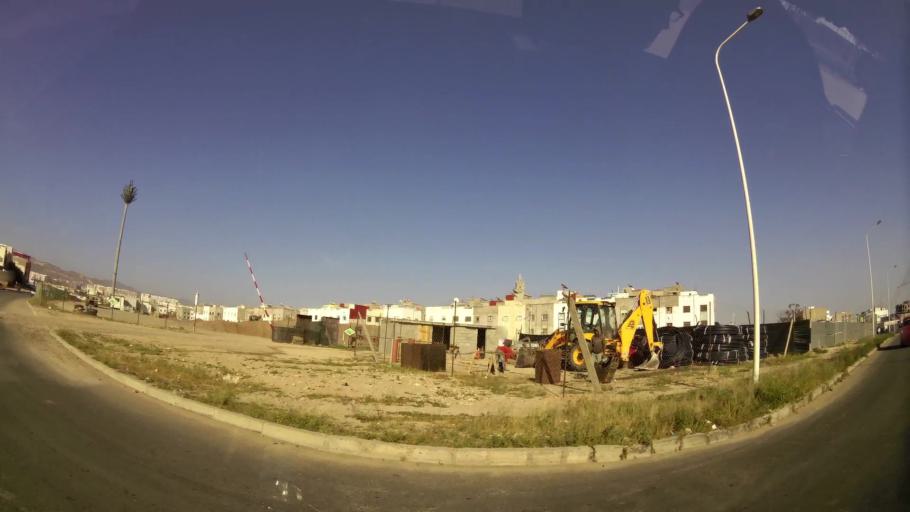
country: MA
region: Souss-Massa-Draa
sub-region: Agadir-Ida-ou-Tnan
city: Agadir
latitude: 30.4237
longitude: -9.5777
